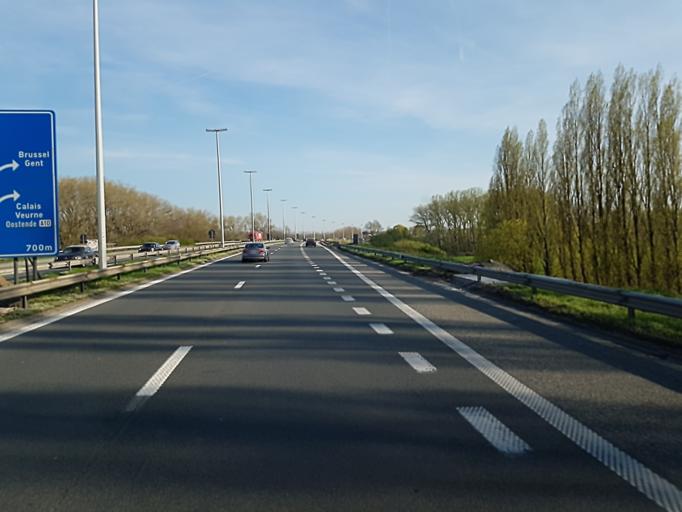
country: BE
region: Flanders
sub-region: Provincie West-Vlaanderen
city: Oostkamp
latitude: 51.1657
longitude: 3.2117
